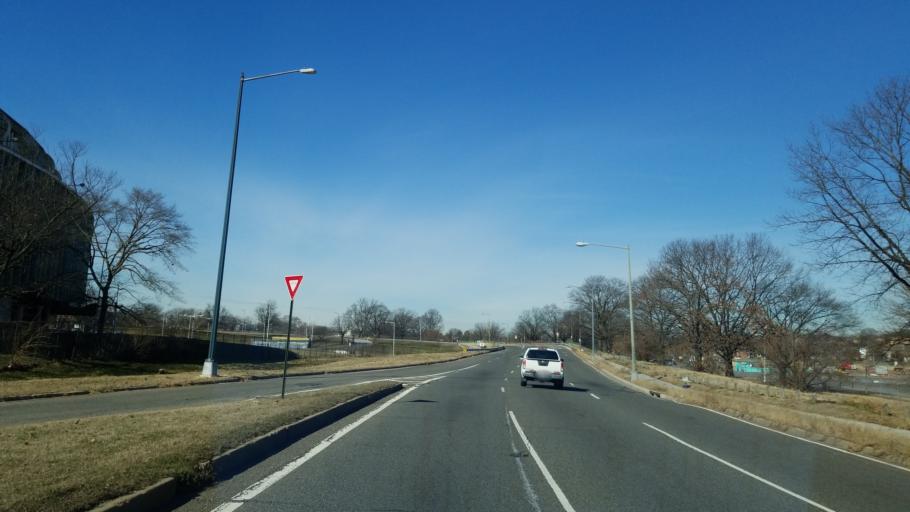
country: US
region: Maryland
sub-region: Prince George's County
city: Colmar Manor
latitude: 38.8904
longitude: -76.9701
